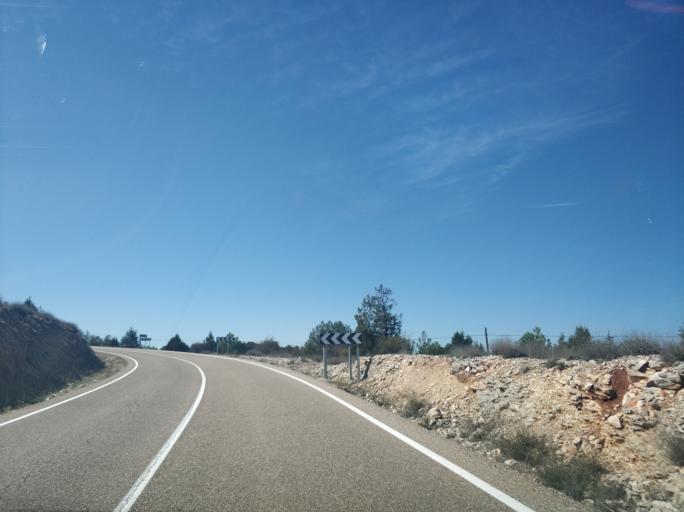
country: ES
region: Castille and Leon
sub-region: Provincia de Soria
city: Santa Maria de las Hoyas
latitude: 41.7837
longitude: -3.1226
